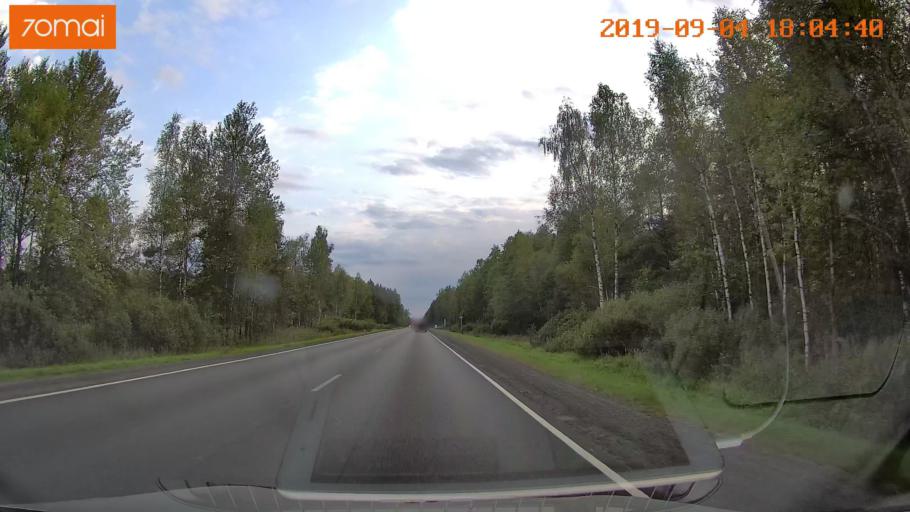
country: RU
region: Moskovskaya
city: Il'inskiy Pogost
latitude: 55.4497
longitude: 38.8361
